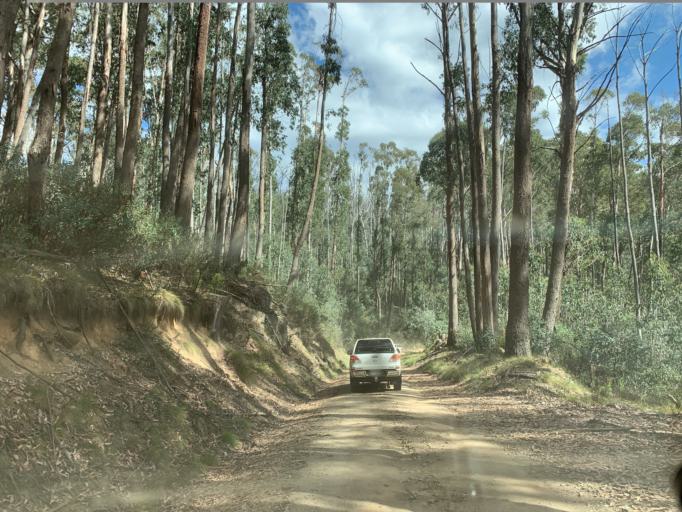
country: AU
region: Victoria
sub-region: Mansfield
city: Mansfield
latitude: -37.0983
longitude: 146.5430
